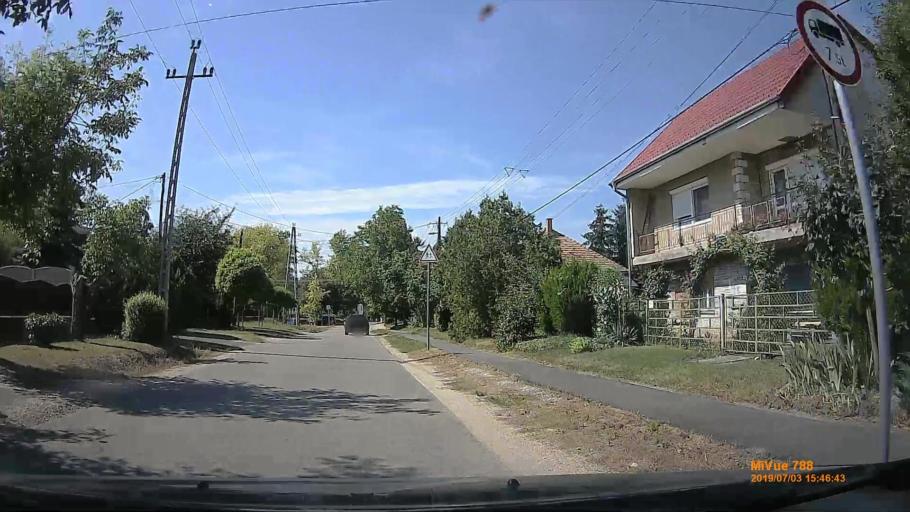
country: HU
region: Gyor-Moson-Sopron
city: Toltestava
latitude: 47.6918
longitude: 17.7476
